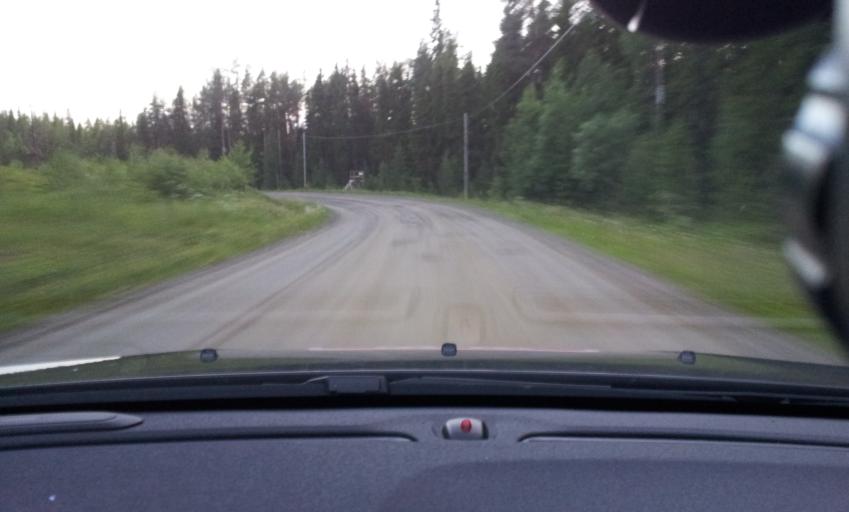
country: SE
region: Jaemtland
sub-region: Ragunda Kommun
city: Hammarstrand
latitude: 62.9189
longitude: 16.1102
